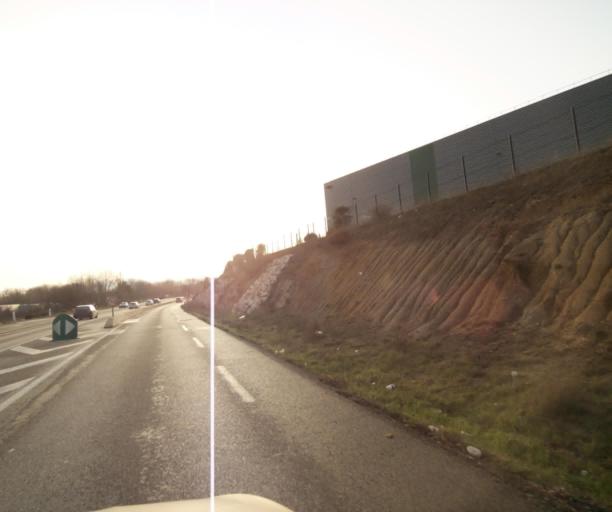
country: FR
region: Provence-Alpes-Cote d'Azur
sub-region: Departement des Bouches-du-Rhone
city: Rousset
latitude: 43.4682
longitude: 5.6007
